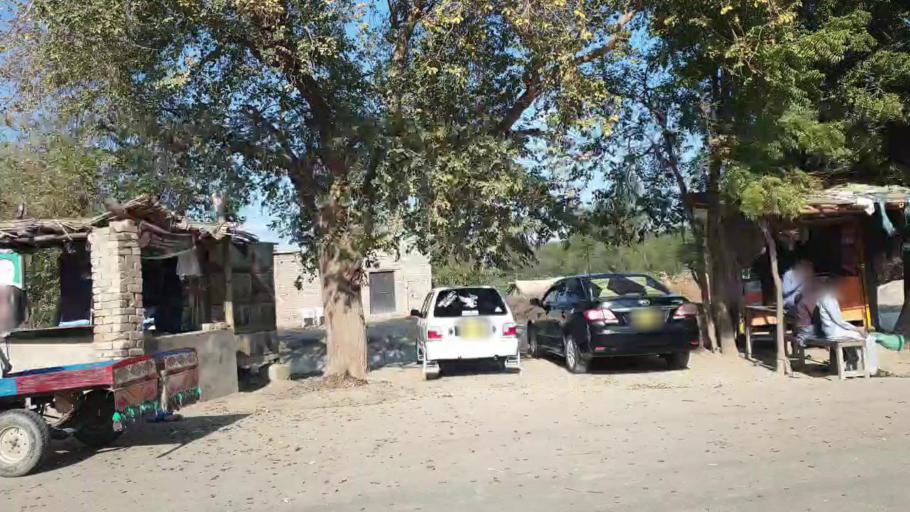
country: PK
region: Sindh
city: Shahpur Chakar
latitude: 26.1112
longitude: 68.5674
